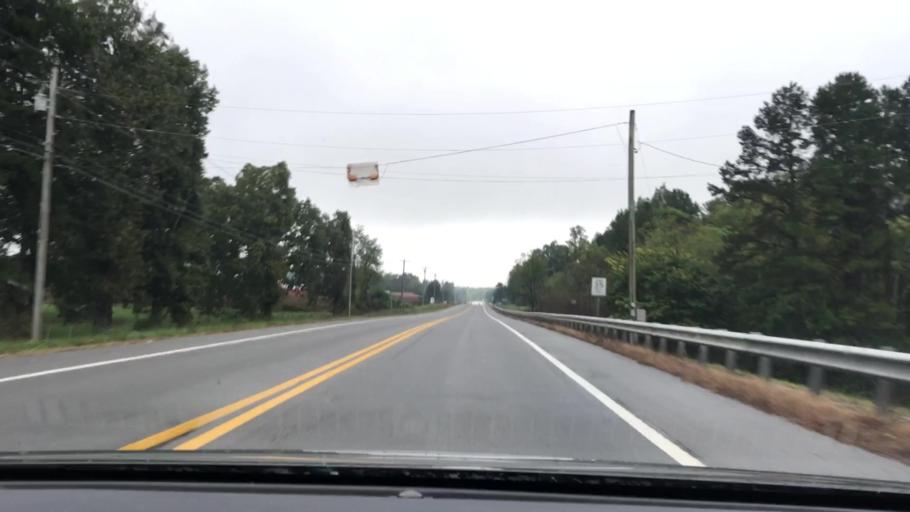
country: US
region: Tennessee
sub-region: Fentress County
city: Grimsley
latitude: 36.2456
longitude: -85.0012
